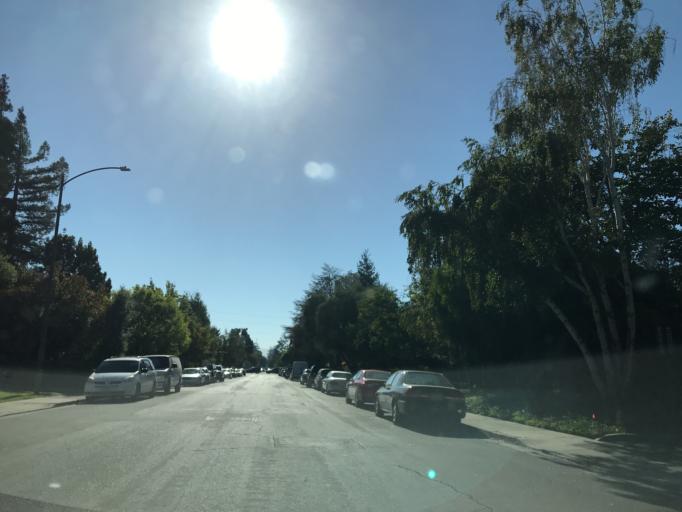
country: US
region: California
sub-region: Santa Clara County
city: Mountain View
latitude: 37.4124
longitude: -122.0903
